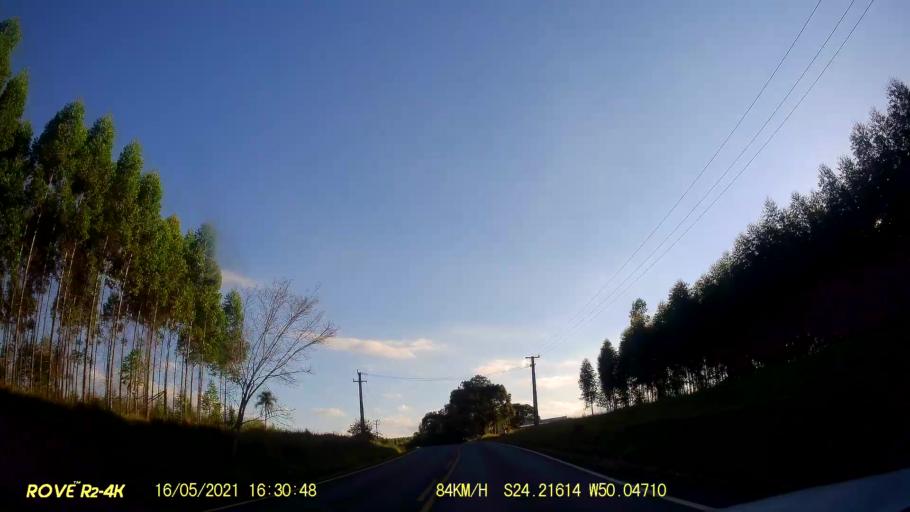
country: BR
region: Parana
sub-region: Pirai Do Sul
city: Pirai do Sul
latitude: -24.2162
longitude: -50.0473
